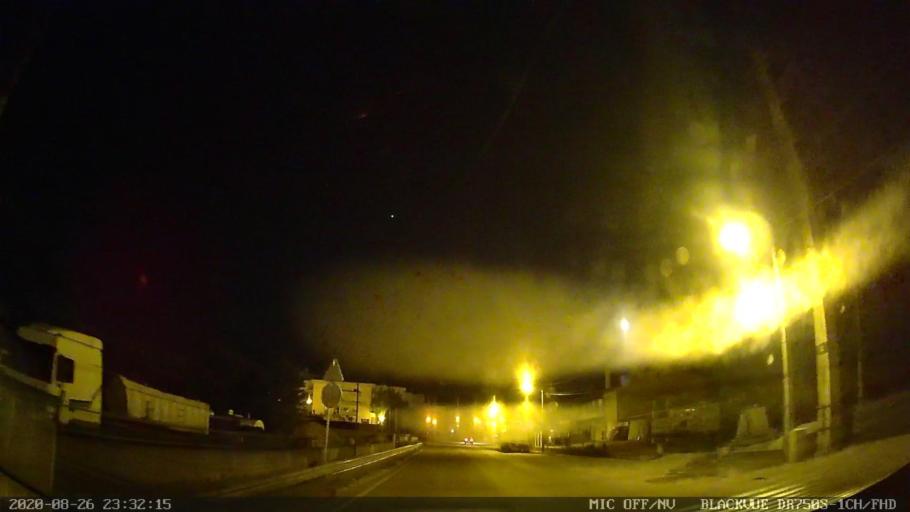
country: PT
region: Viseu
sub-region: Viseu
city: Rio de Loba
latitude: 40.6732
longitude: -7.8865
